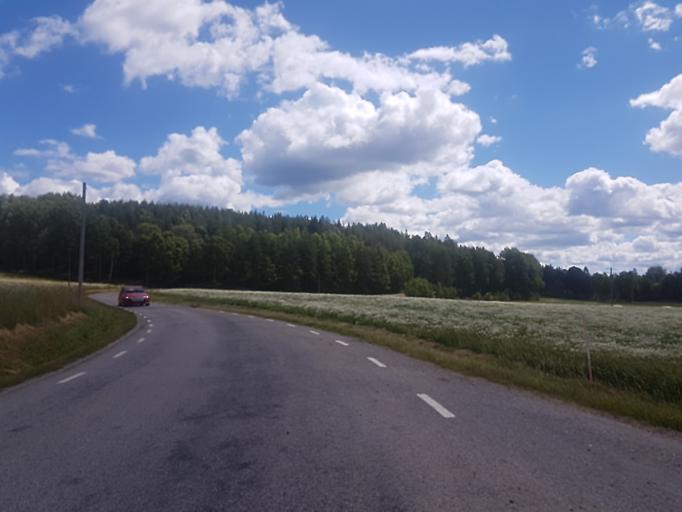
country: SE
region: Soedermanland
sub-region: Gnesta Kommun
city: Gnesta
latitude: 59.0407
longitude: 17.3443
